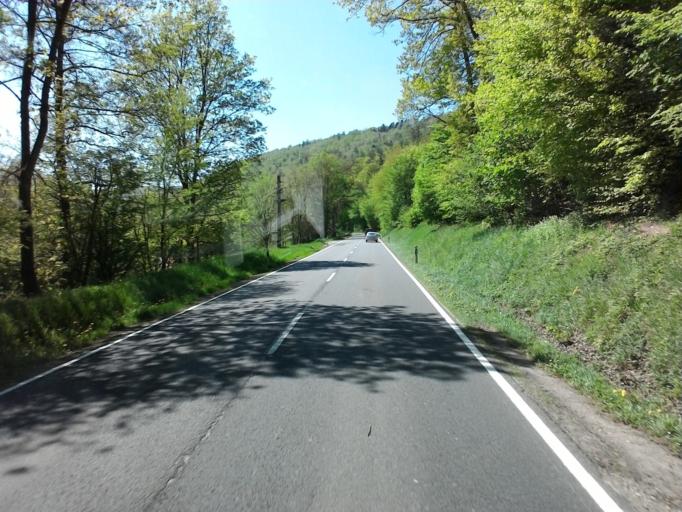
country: DE
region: Bavaria
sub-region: Regierungsbezirk Unterfranken
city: Lohr am Main
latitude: 49.9815
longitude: 9.5416
